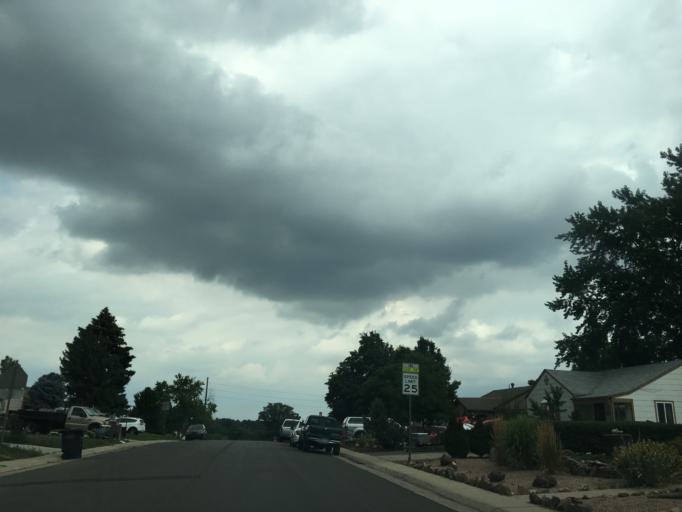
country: US
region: Colorado
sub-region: Arapahoe County
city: Sheridan
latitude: 39.6843
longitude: -105.0110
